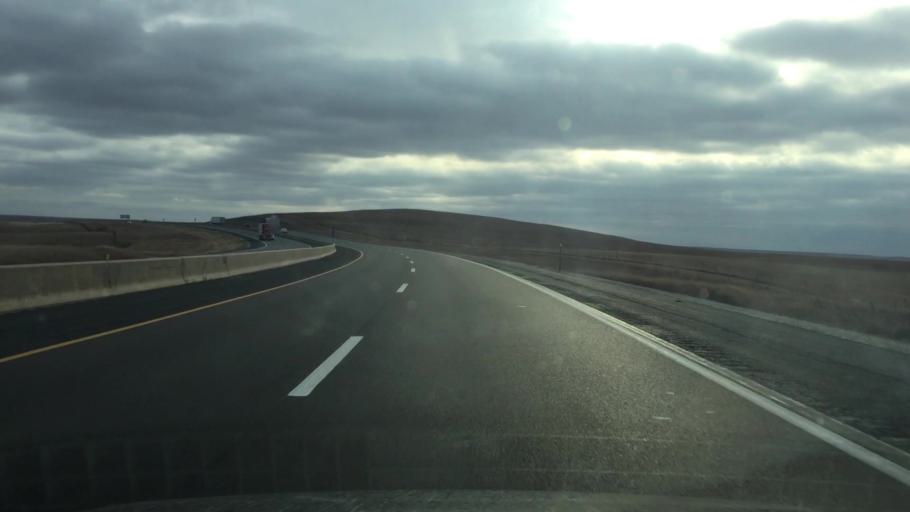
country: US
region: Kansas
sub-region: Chase County
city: Cottonwood Falls
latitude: 38.2193
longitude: -96.4331
